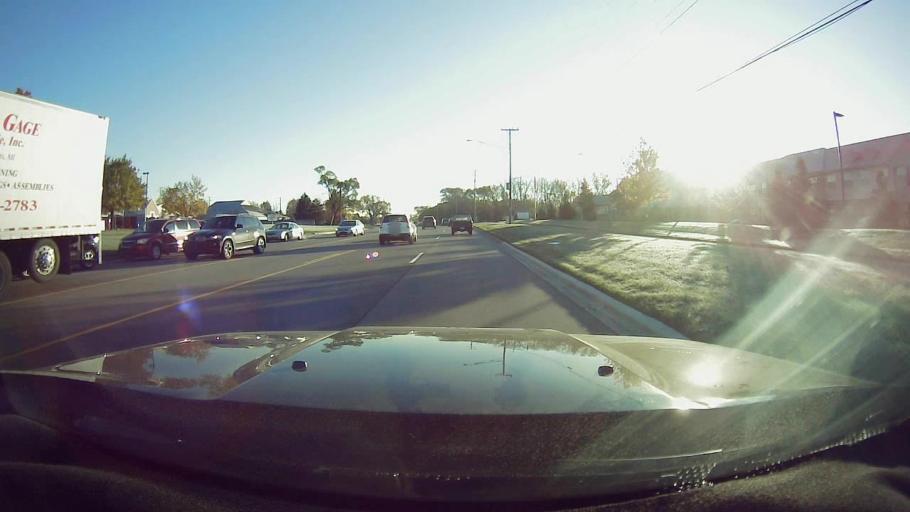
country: US
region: Michigan
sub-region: Oakland County
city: Clawson
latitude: 42.5494
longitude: -83.0863
